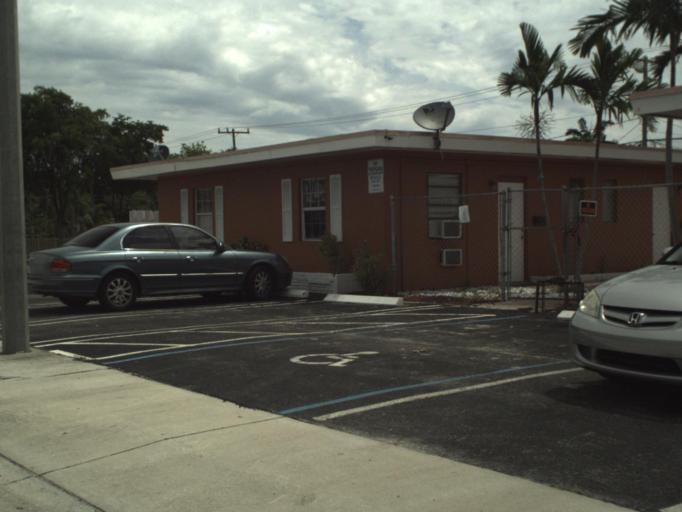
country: US
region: Florida
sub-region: Palm Beach County
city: Mangonia Park
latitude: 26.7426
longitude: -80.0566
